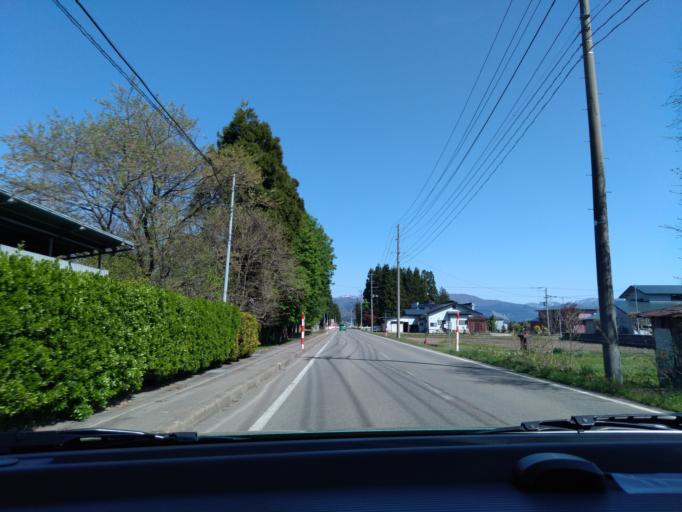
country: JP
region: Akita
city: Kakunodatemachi
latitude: 39.5757
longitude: 140.5694
